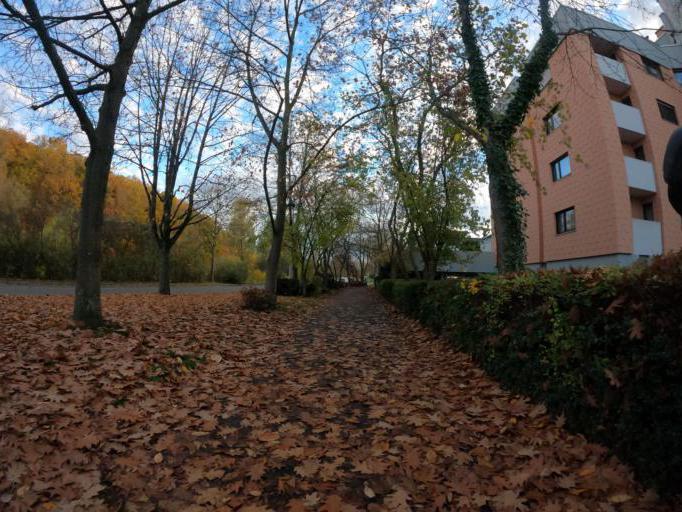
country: DE
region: Baden-Wuerttemberg
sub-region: Regierungsbezirk Stuttgart
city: Magstadt
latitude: 48.7223
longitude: 8.9882
